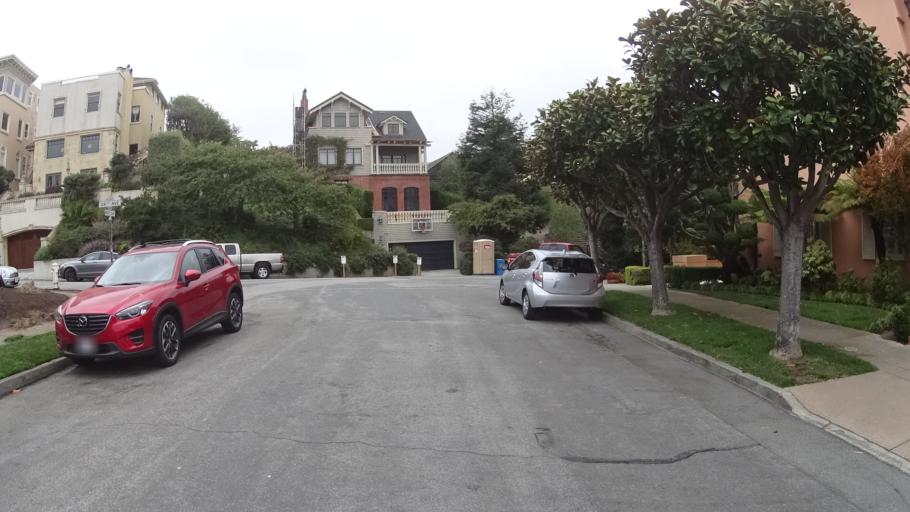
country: US
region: California
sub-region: San Francisco County
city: San Francisco
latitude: 37.7869
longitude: -122.4838
